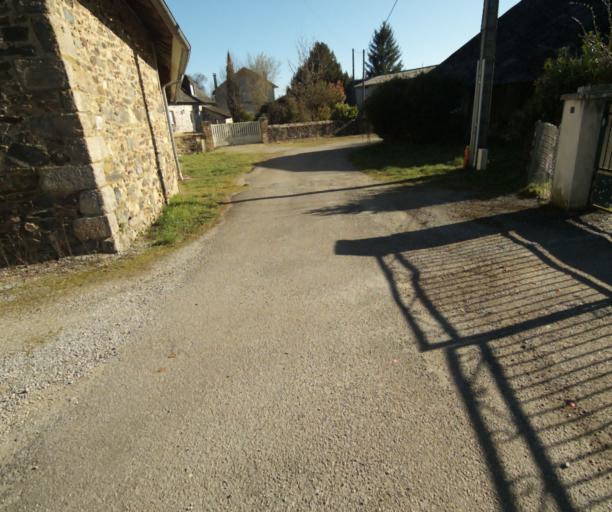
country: FR
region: Limousin
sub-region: Departement de la Correze
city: Seilhac
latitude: 45.3869
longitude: 1.7297
